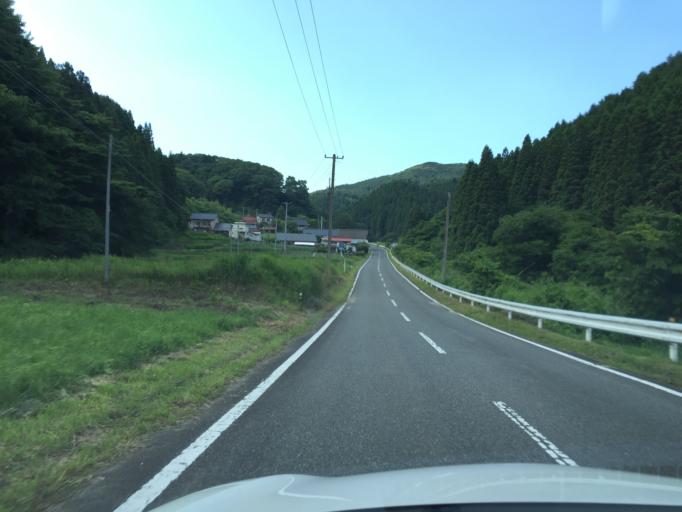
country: JP
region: Fukushima
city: Ishikawa
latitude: 37.1306
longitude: 140.6423
